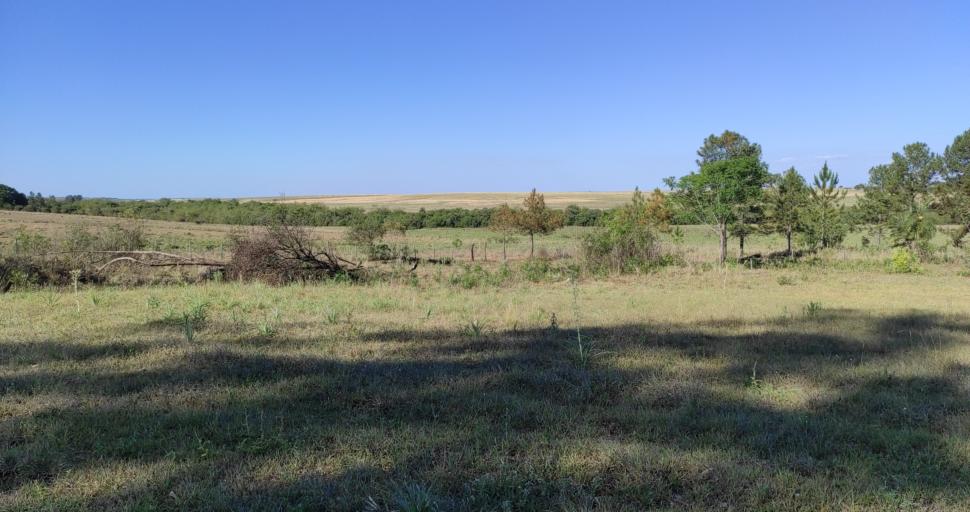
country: PY
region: Itapua
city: San Juan del Parana
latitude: -27.4545
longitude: -56.0561
